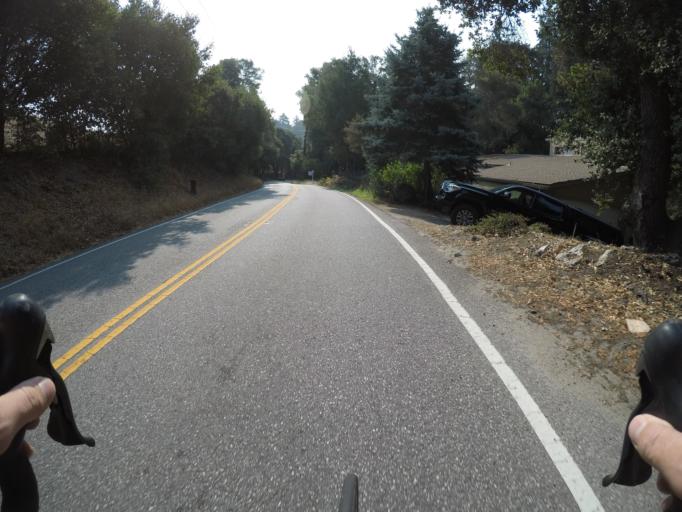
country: US
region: California
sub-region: Santa Cruz County
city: Pasatiempo
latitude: 37.0015
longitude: -122.0102
